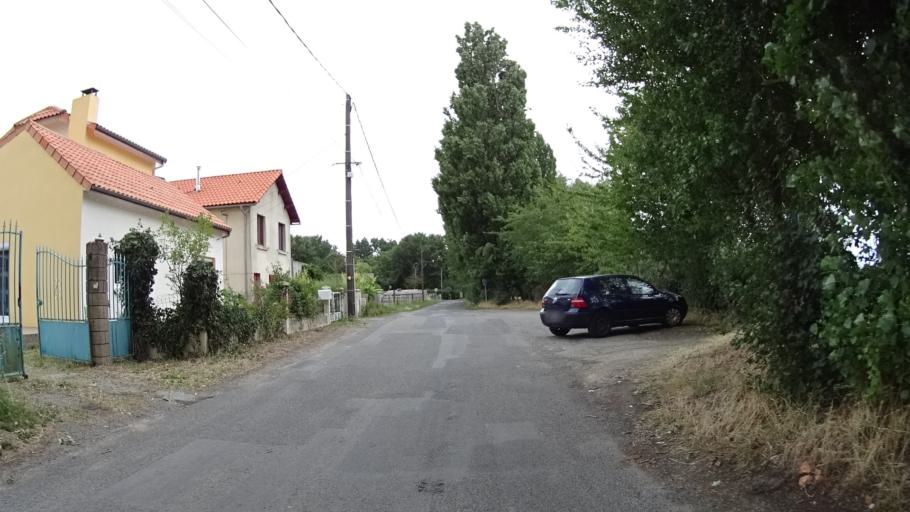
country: FR
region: Pays de la Loire
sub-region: Departement de la Loire-Atlantique
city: Sainte-Luce-sur-Loire
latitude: 47.2419
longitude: -1.4656
